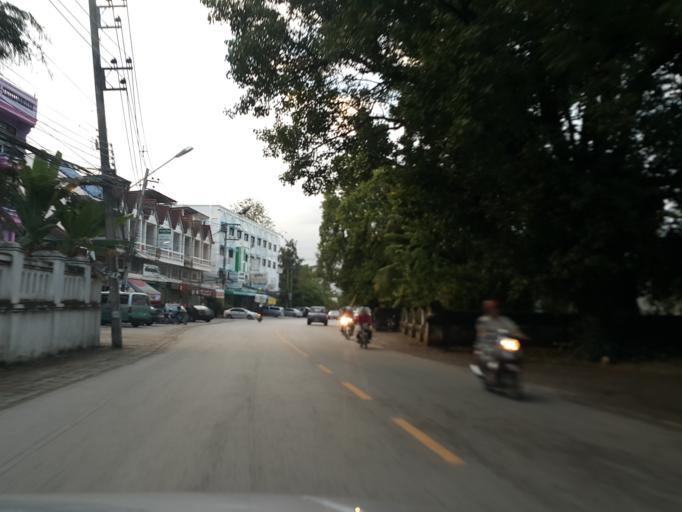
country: TH
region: Lampang
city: Lampang
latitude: 18.2838
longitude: 99.5053
